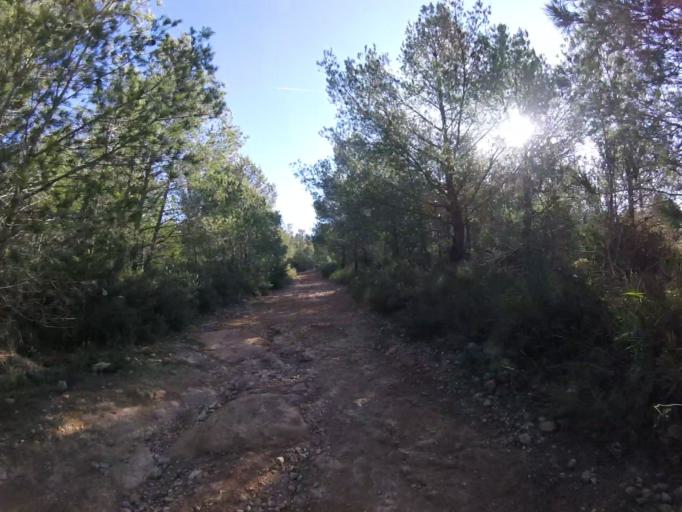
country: ES
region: Valencia
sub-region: Provincia de Castello
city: Benicassim
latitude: 40.0894
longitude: 0.0992
